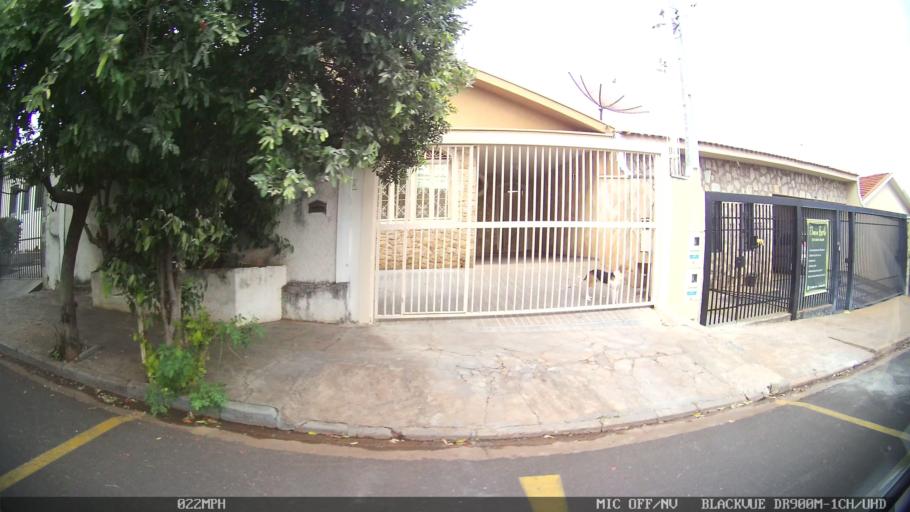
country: BR
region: Sao Paulo
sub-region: Sao Jose Do Rio Preto
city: Sao Jose do Rio Preto
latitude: -20.8149
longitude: -49.3646
